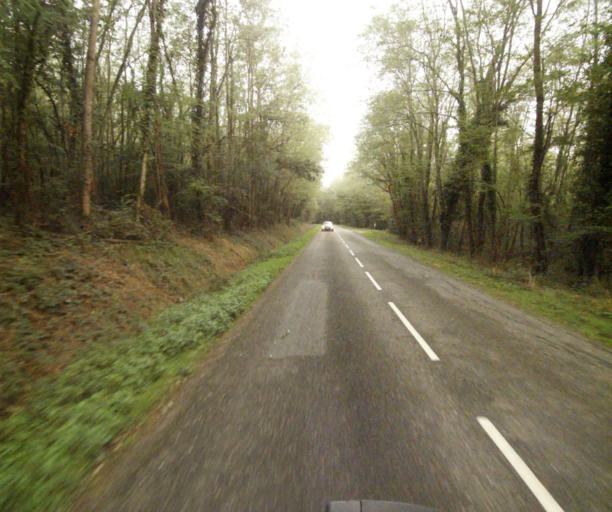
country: FR
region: Midi-Pyrenees
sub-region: Departement du Tarn-et-Garonne
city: Saint-Nauphary
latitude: 43.9354
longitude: 1.4634
